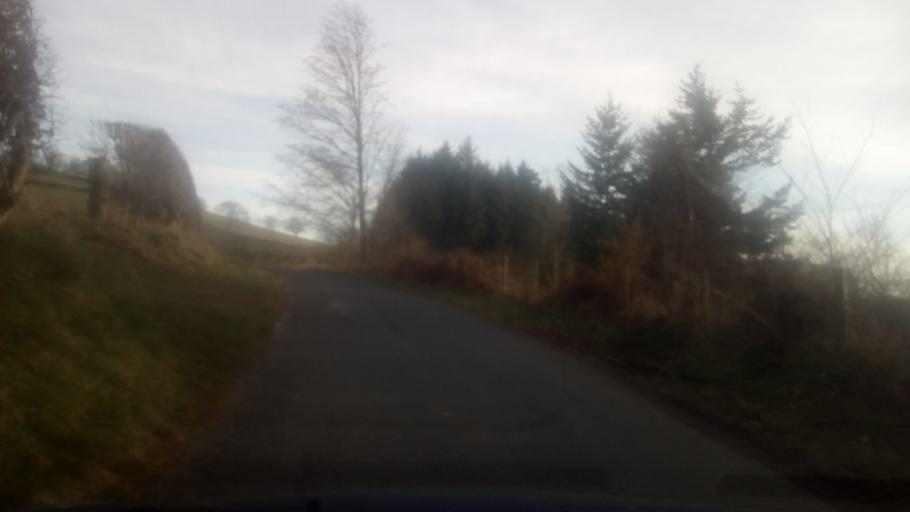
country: GB
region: Scotland
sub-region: The Scottish Borders
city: Jedburgh
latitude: 55.4476
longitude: -2.6344
